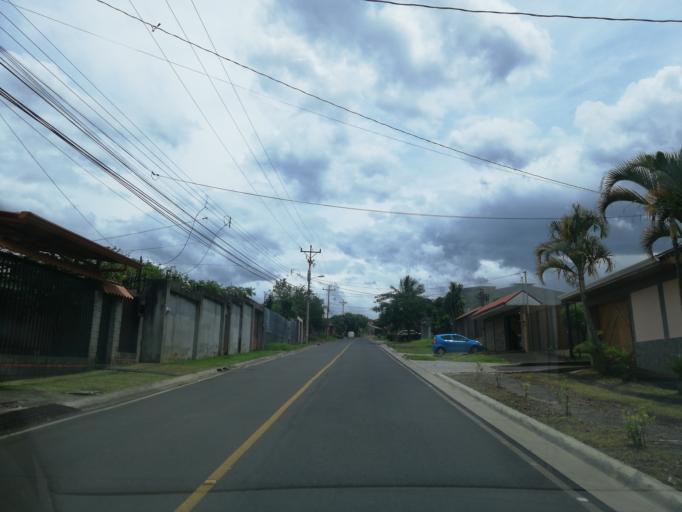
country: CR
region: Alajuela
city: Alajuela
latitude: 10.0264
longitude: -84.1968
